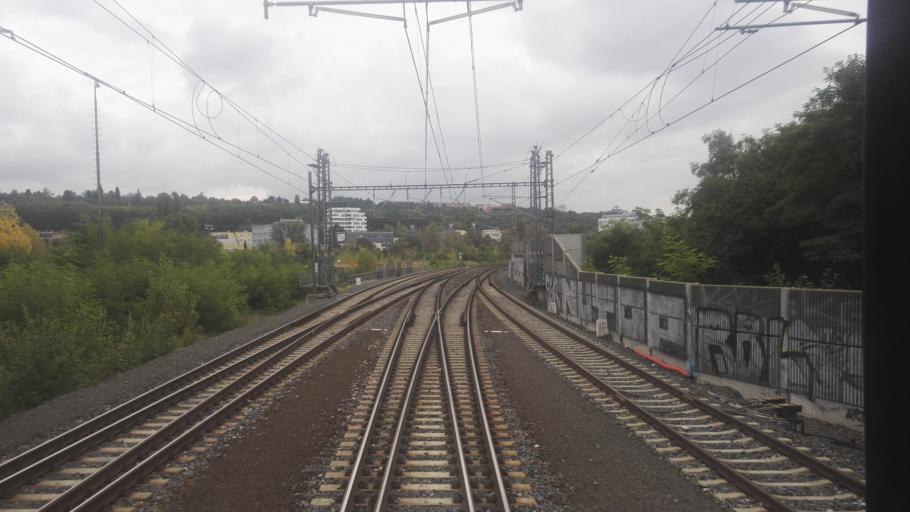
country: CZ
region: Praha
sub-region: Praha 8
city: Liben
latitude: 50.1024
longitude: 14.4806
